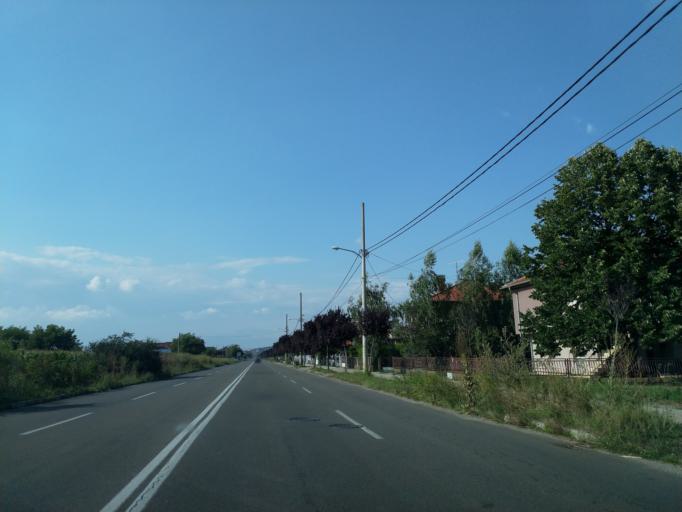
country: RS
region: Central Serbia
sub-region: Pomoravski Okrug
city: Paracin
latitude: 43.8387
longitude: 21.4155
